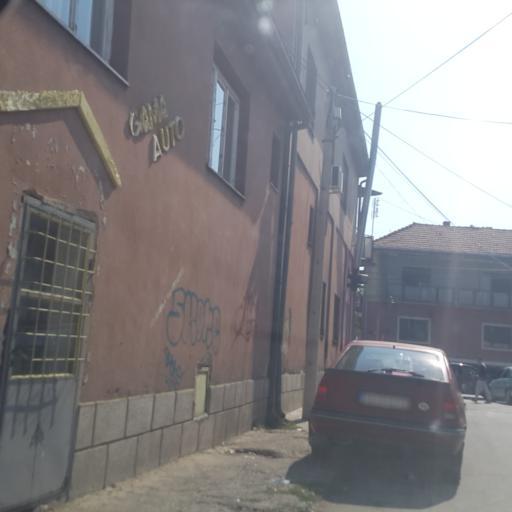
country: RS
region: Central Serbia
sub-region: Zajecarski Okrug
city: Zajecar
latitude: 43.9047
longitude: 22.2822
